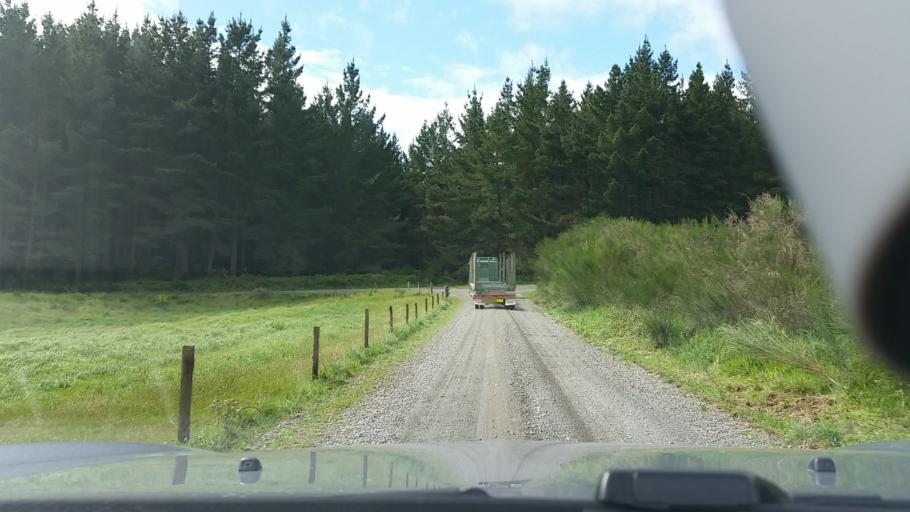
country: NZ
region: Bay of Plenty
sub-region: Whakatane District
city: Murupara
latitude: -38.3452
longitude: 176.5440
